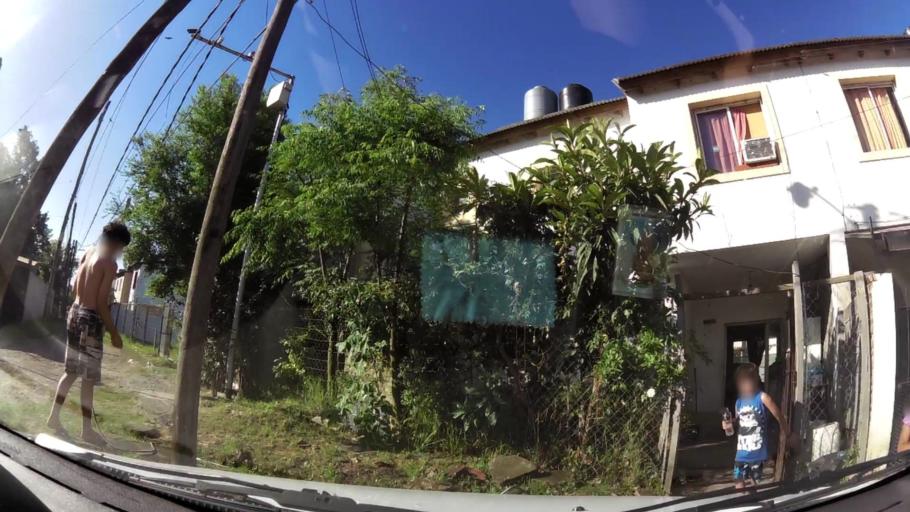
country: AR
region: Buenos Aires
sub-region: Partido de San Isidro
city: San Isidro
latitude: -34.4666
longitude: -58.5007
